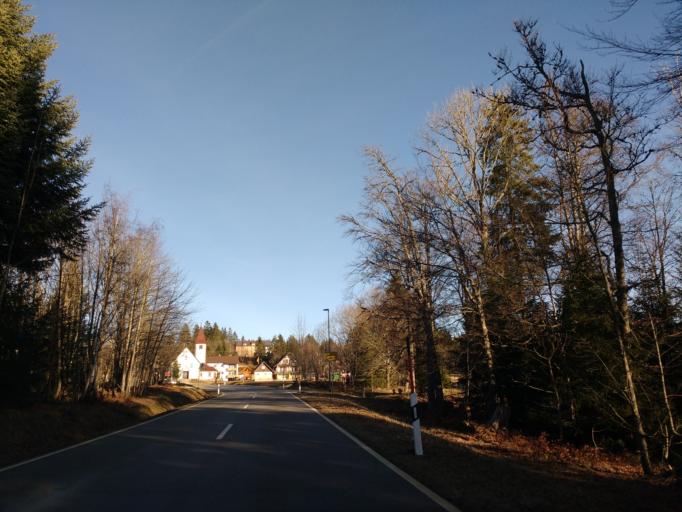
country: DE
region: Baden-Wuerttemberg
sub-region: Karlsruhe Region
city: Bad Rippoldsau-Schapbach
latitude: 48.4643
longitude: 8.2989
